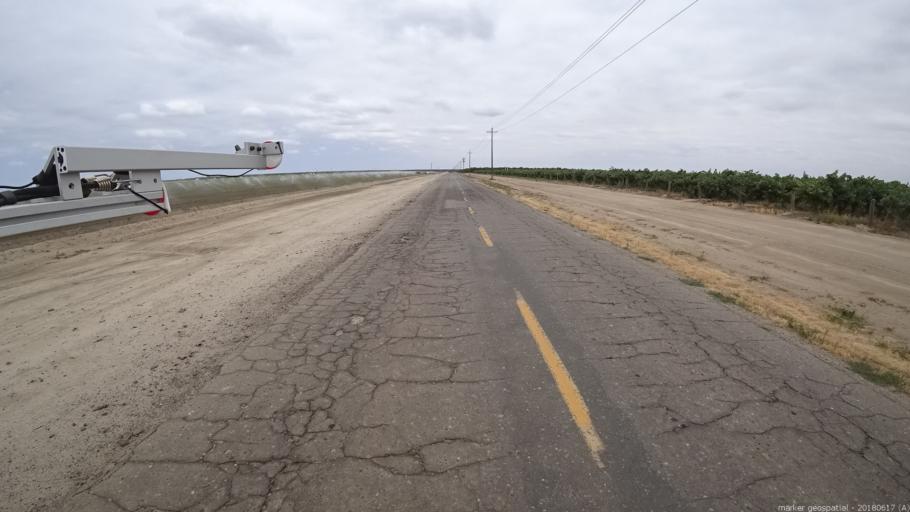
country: US
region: California
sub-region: Madera County
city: Madera
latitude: 36.9105
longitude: -120.1652
